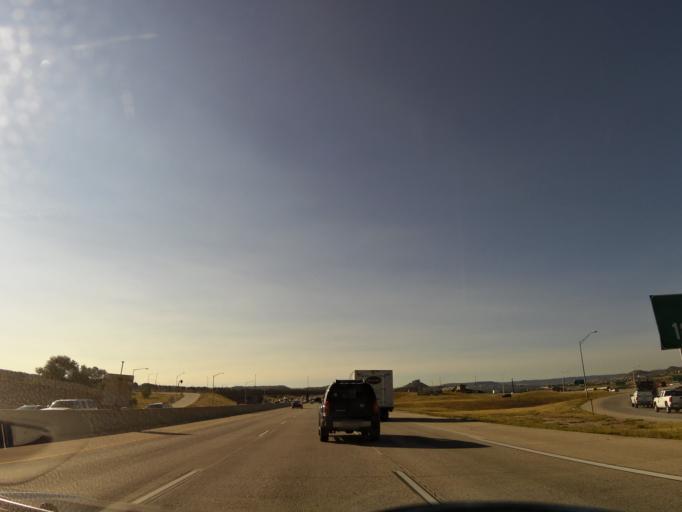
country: US
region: Colorado
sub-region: Douglas County
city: Castle Rock
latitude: 39.4155
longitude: -104.8701
